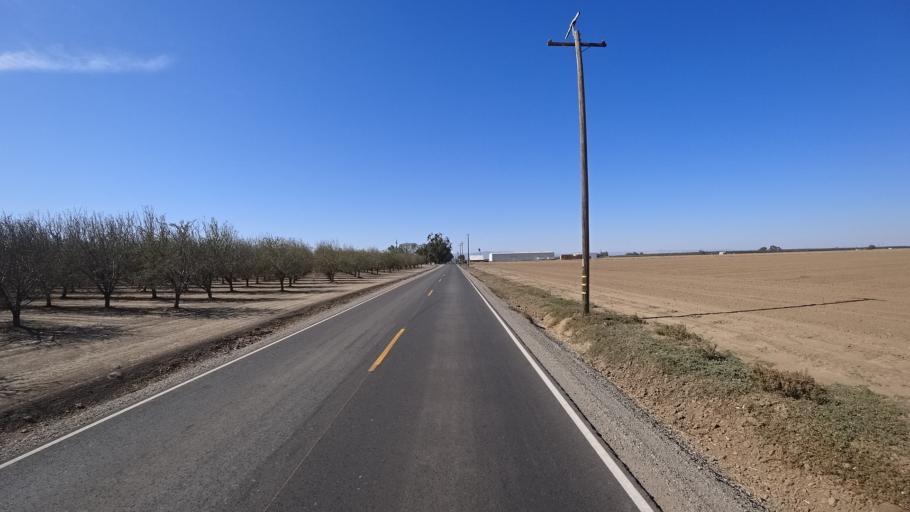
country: US
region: California
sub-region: Yolo County
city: Woodland
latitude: 38.6196
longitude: -121.8096
